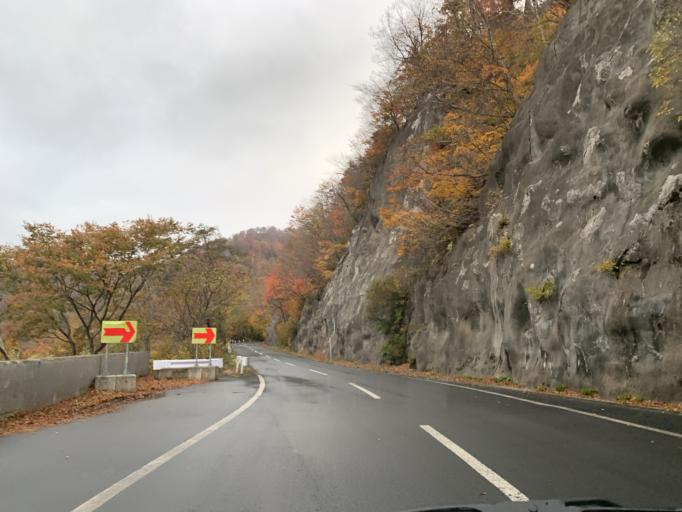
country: JP
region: Iwate
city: Mizusawa
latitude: 39.1126
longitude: 140.8466
